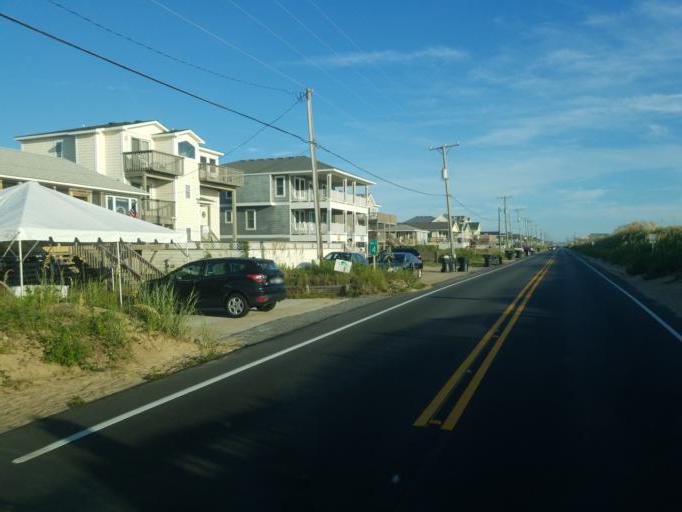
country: US
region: North Carolina
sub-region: Dare County
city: Kitty Hawk
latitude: 36.0711
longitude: -75.6932
